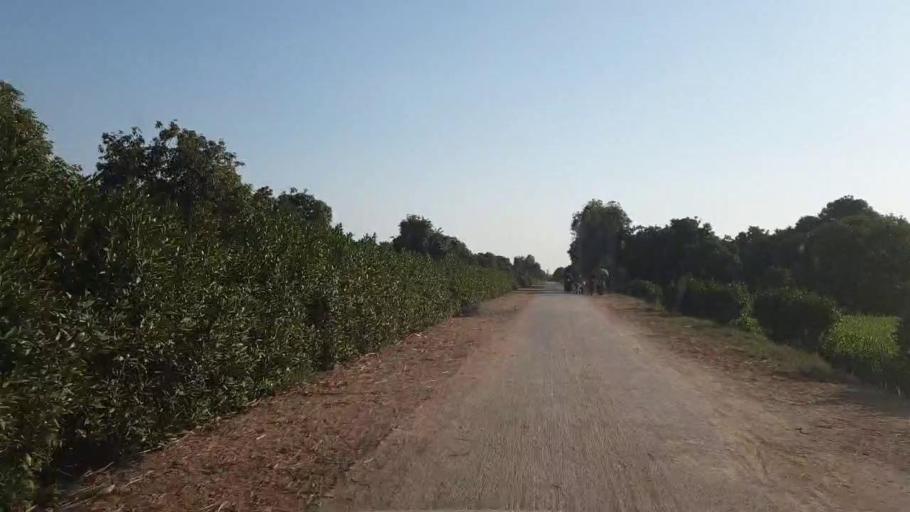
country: PK
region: Sindh
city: Tando Allahyar
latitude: 25.3665
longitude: 68.6825
